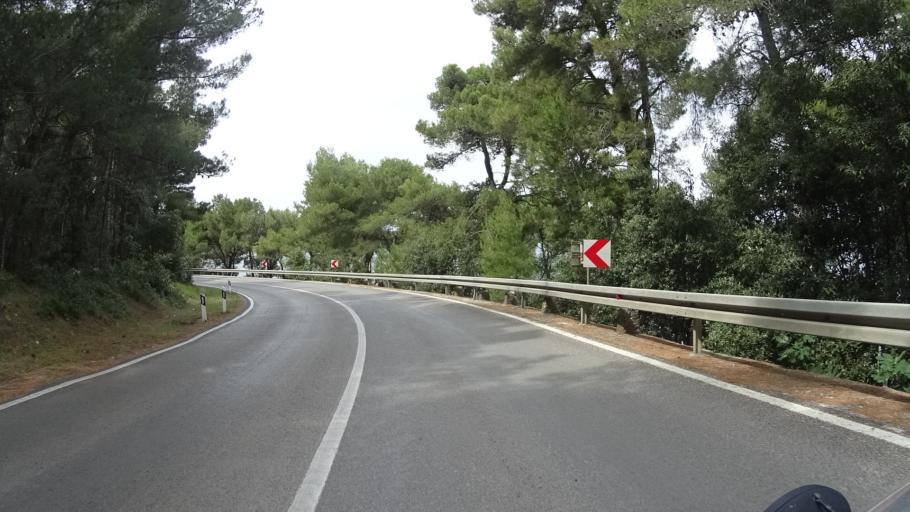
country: HR
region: Istarska
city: Medulin
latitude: 44.8138
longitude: 13.9128
